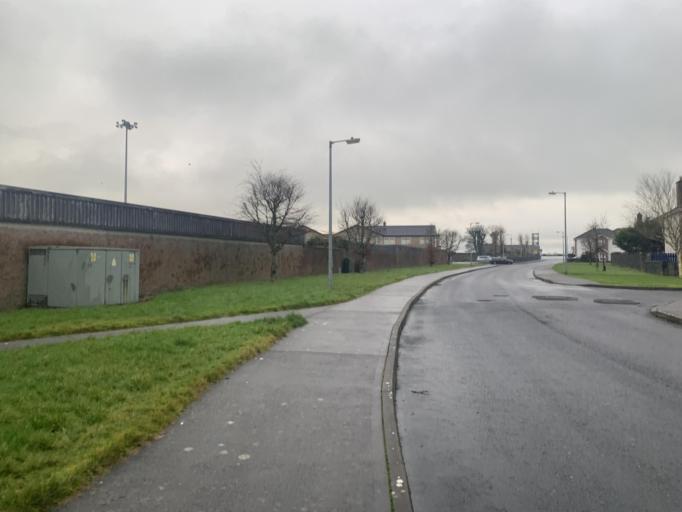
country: IE
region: Connaught
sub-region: County Galway
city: Tuam
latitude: 53.5267
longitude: -8.8537
